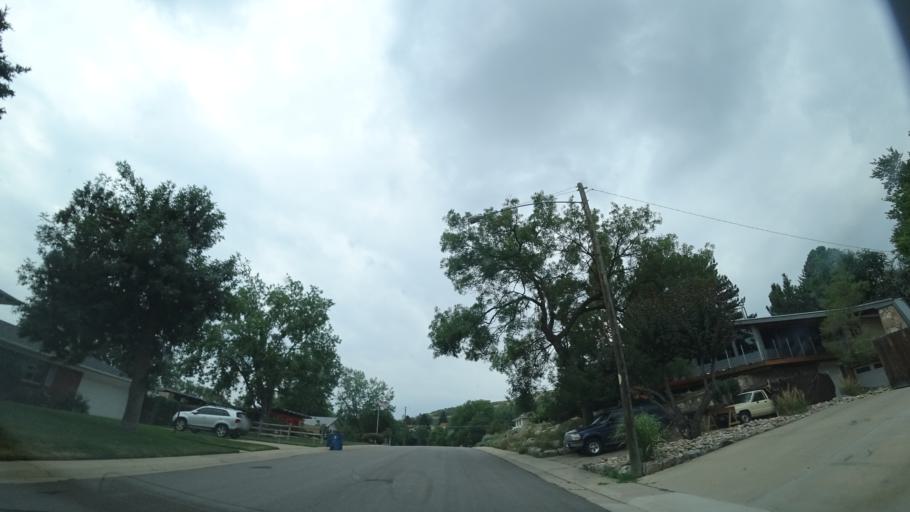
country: US
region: Colorado
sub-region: Jefferson County
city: West Pleasant View
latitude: 39.6991
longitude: -105.1517
